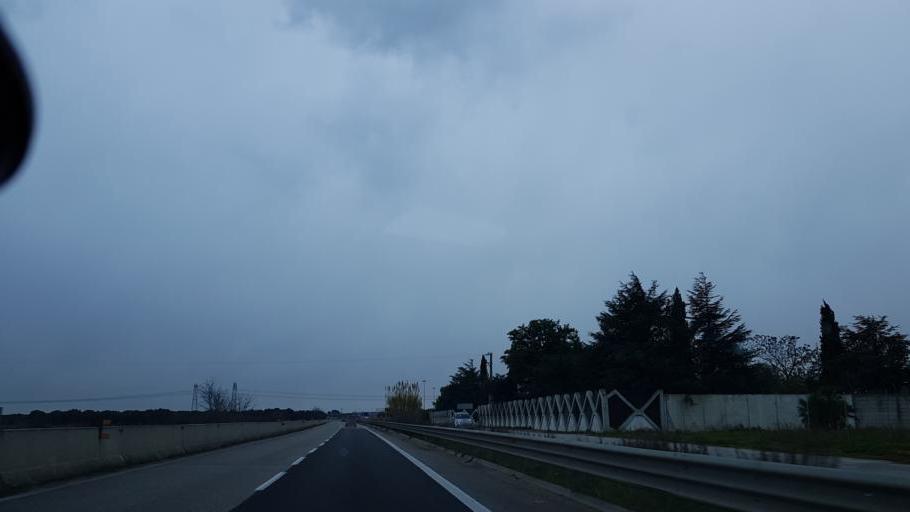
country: IT
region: Apulia
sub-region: Provincia di Brindisi
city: Mesagne
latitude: 40.5820
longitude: 17.8441
